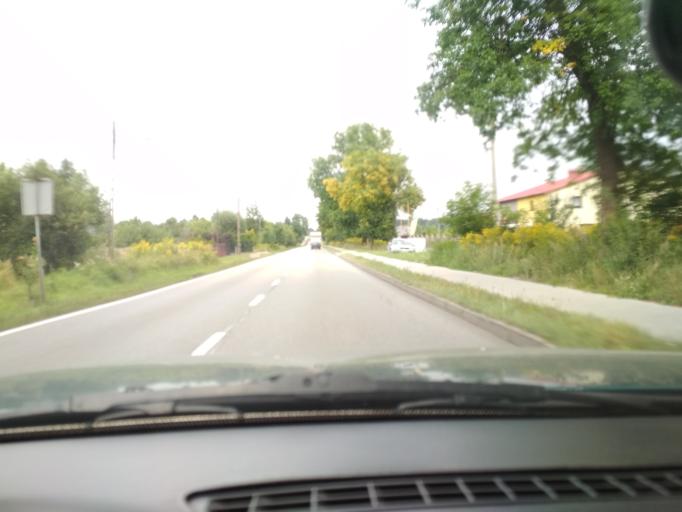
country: PL
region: Silesian Voivodeship
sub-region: Powiat zawiercianski
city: Lazy
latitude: 50.4539
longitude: 19.3765
